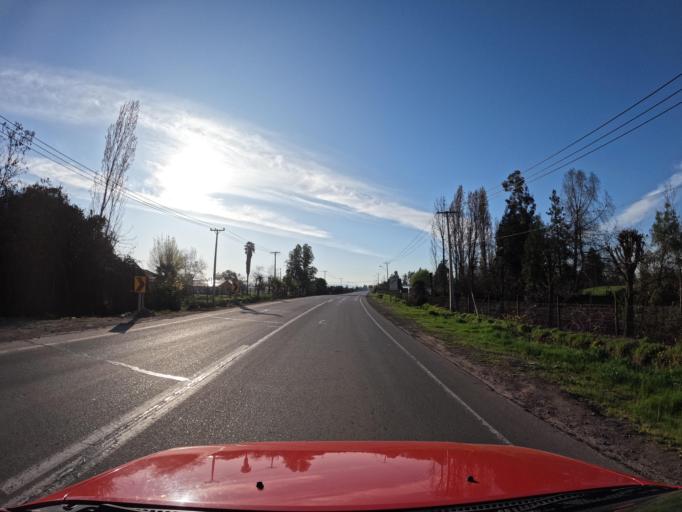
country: CL
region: Maule
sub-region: Provincia de Curico
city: Teno
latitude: -34.8848
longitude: -71.0758
